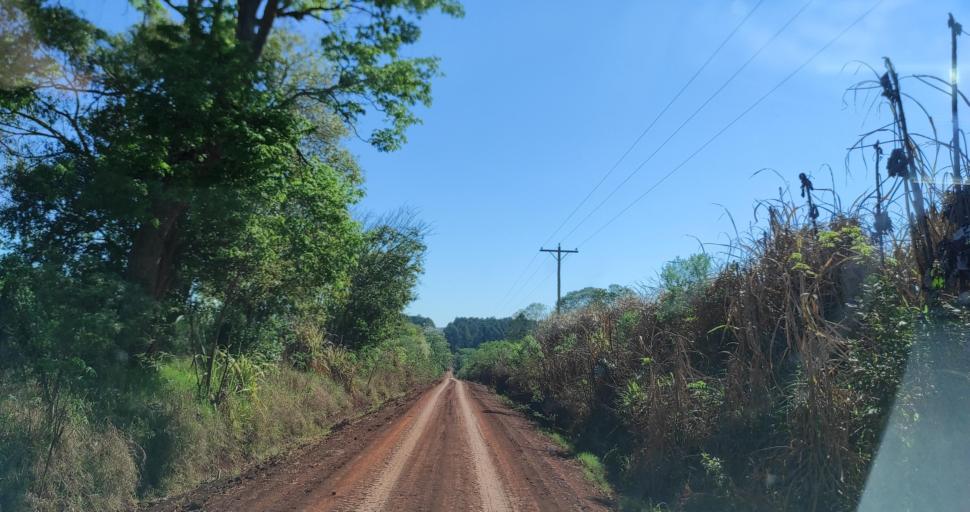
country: AR
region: Misiones
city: Capiovi
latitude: -26.9165
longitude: -55.0248
